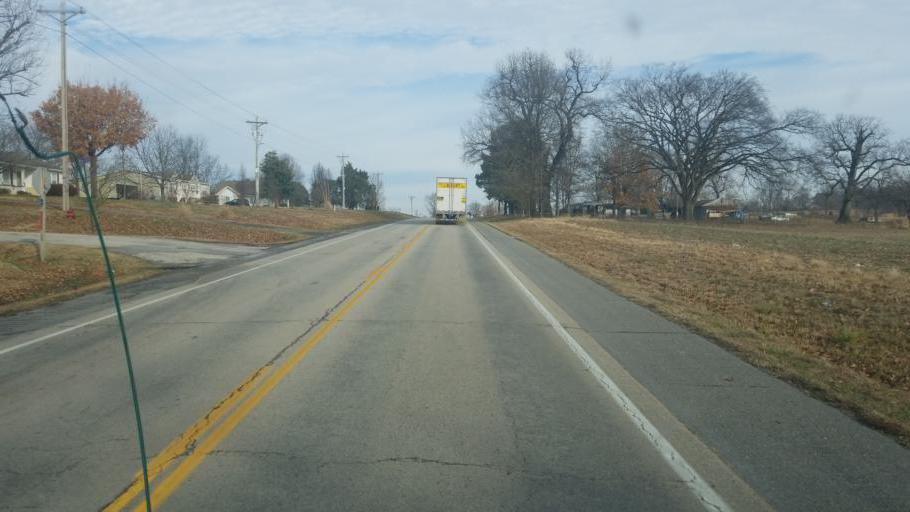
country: US
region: Missouri
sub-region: Stoddard County
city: Bloomfield
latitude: 36.9068
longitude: -89.9223
